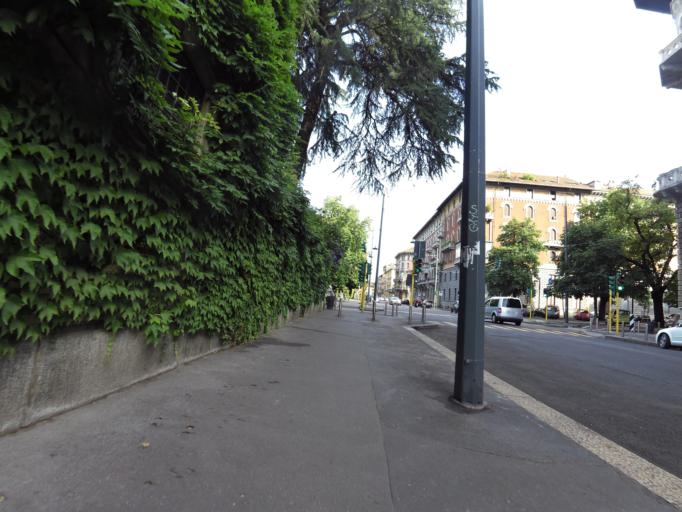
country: IT
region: Lombardy
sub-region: Citta metropolitana di Milano
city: Milano
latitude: 45.4687
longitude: 9.1674
